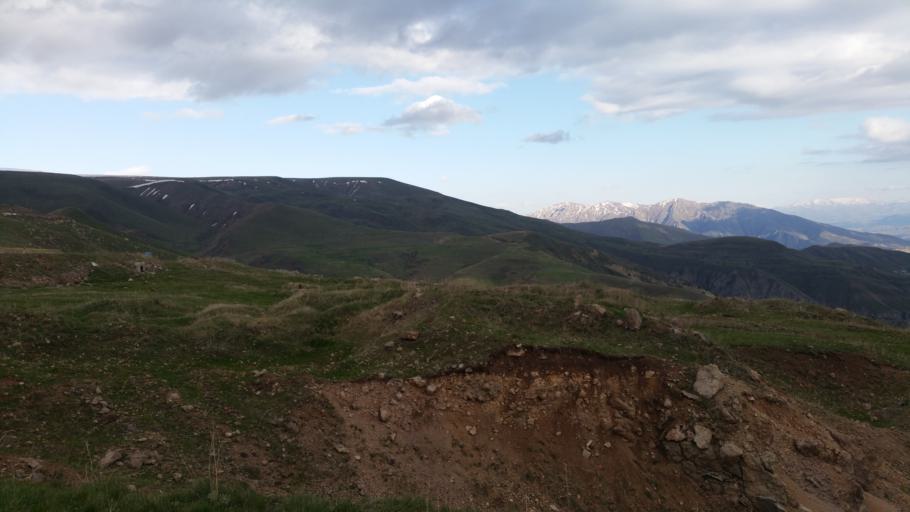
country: AM
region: Geghark'unik'i Marz
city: Madina
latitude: 39.9513
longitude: 45.2332
